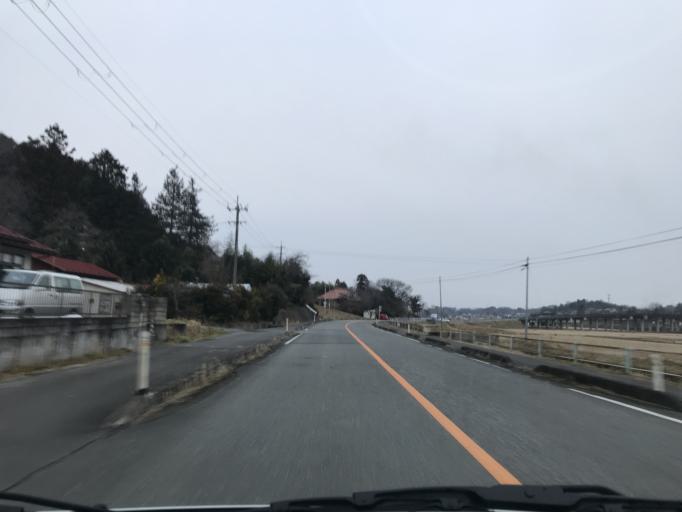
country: JP
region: Miyagi
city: Wakuya
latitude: 38.7068
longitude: 141.1089
